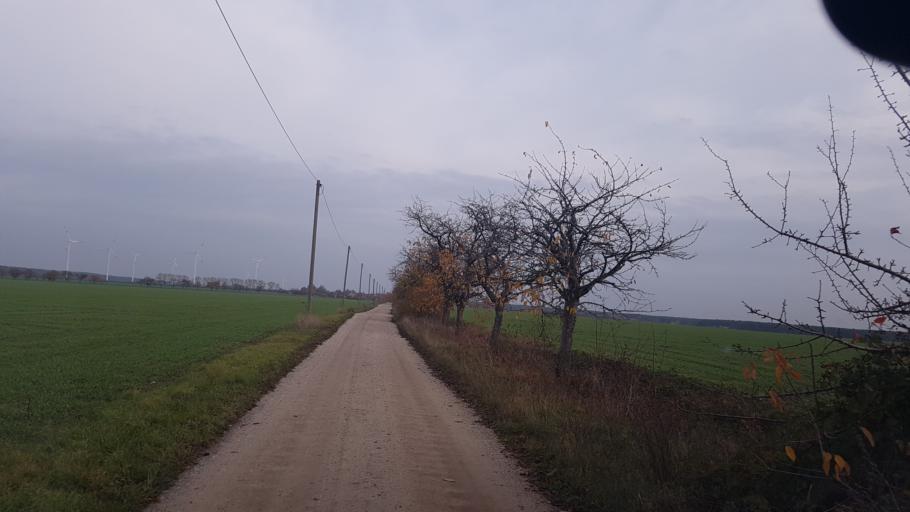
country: DE
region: Brandenburg
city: Trobitz
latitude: 51.6609
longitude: 13.4139
